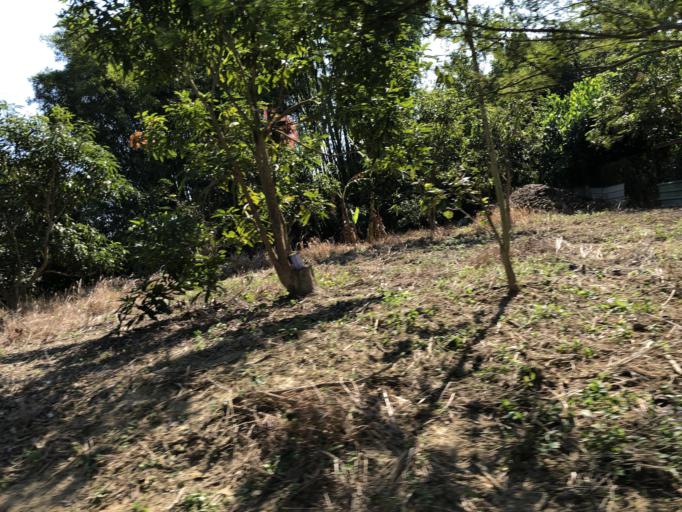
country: TW
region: Taiwan
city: Yujing
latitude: 23.0473
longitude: 120.3674
